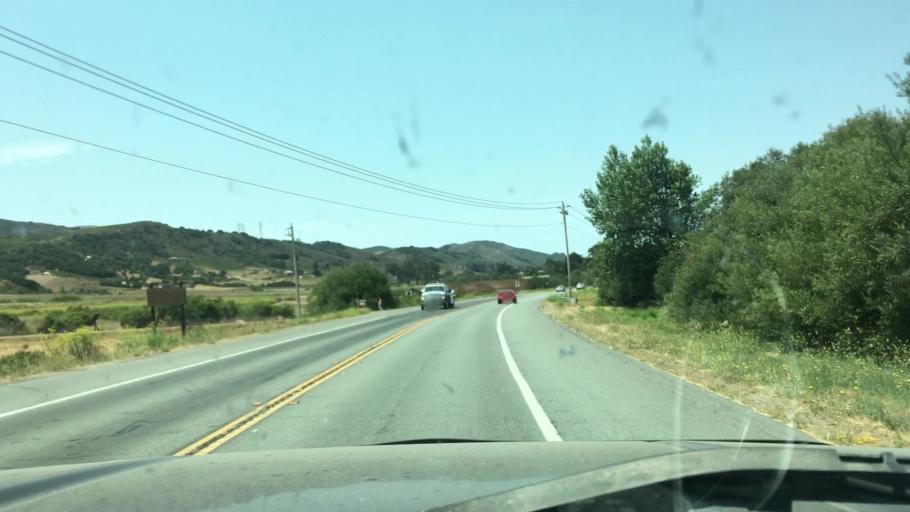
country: US
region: California
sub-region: San Luis Obispo County
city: Los Osos
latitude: 35.2989
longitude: -120.7826
